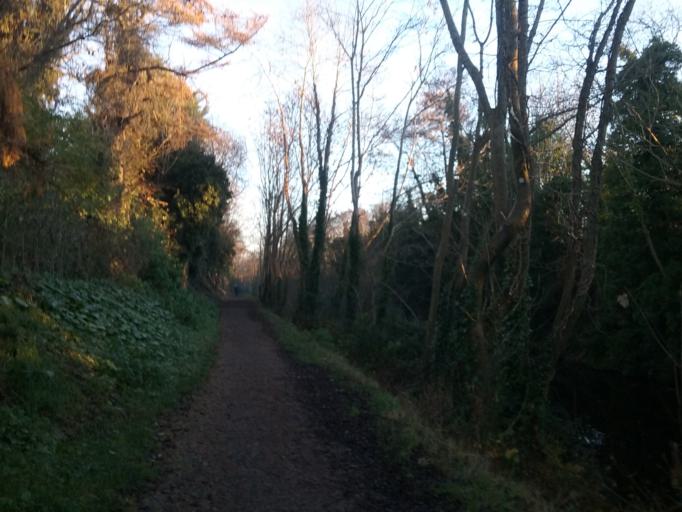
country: IE
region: Leinster
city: Hartstown
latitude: 53.3825
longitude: -6.4205
